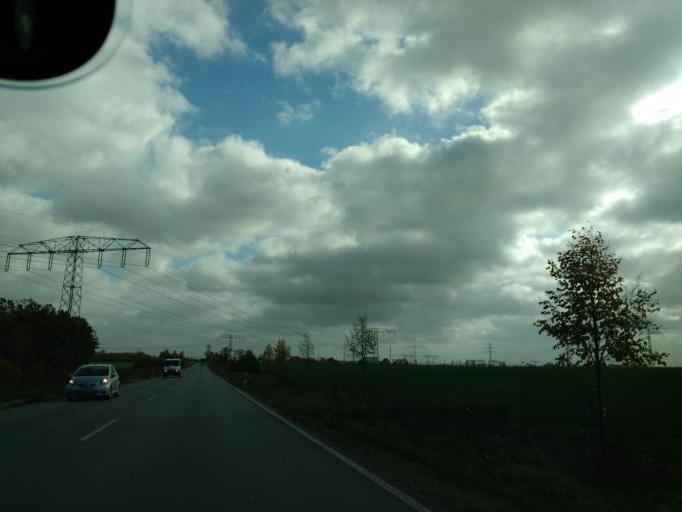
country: DE
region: Brandenburg
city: Neuenhagen
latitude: 52.5493
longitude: 13.7005
